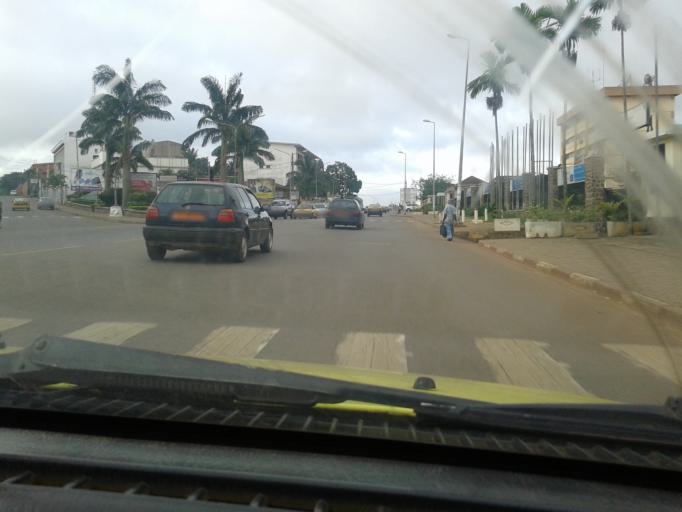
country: CM
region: Centre
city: Yaounde
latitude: 3.8789
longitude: 11.5159
